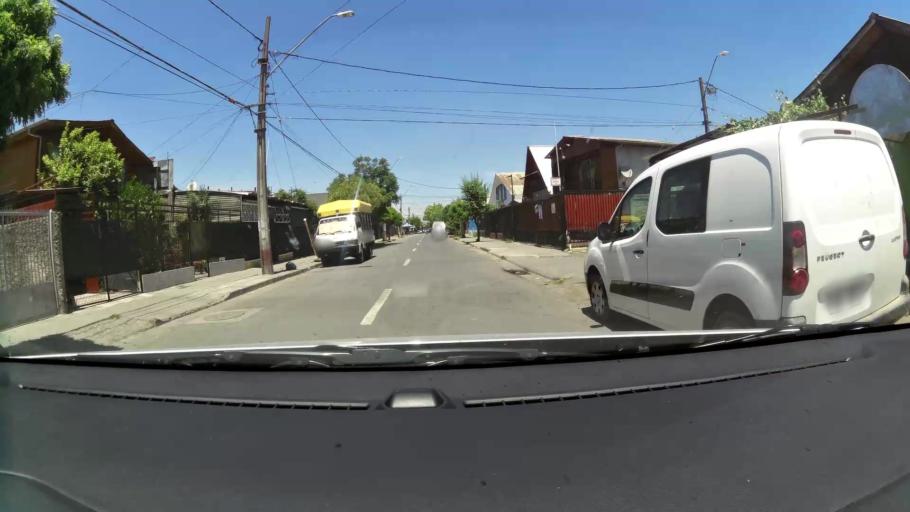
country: CL
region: Santiago Metropolitan
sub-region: Provincia de Santiago
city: La Pintana
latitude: -33.5588
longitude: -70.6427
